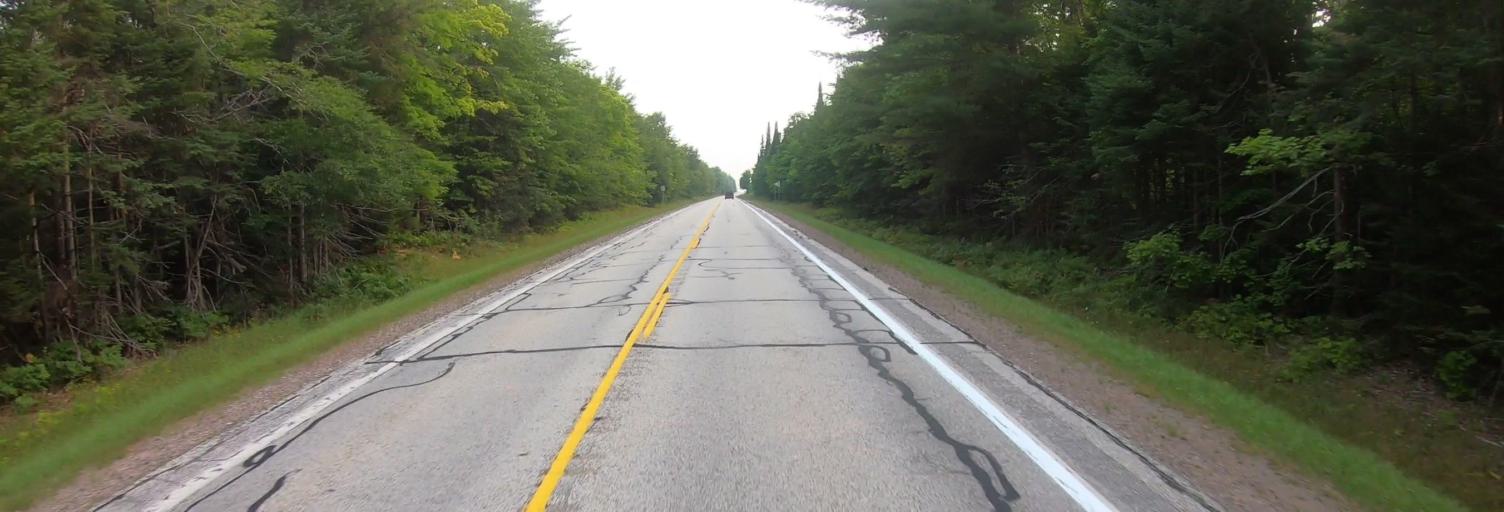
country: US
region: Michigan
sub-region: Luce County
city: Newberry
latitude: 46.4895
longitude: -85.0991
